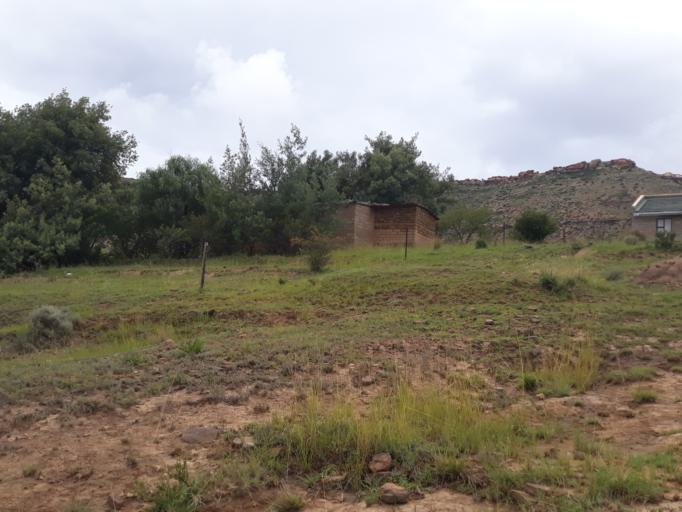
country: LS
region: Quthing
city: Quthing
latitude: -30.3326
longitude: 27.5309
